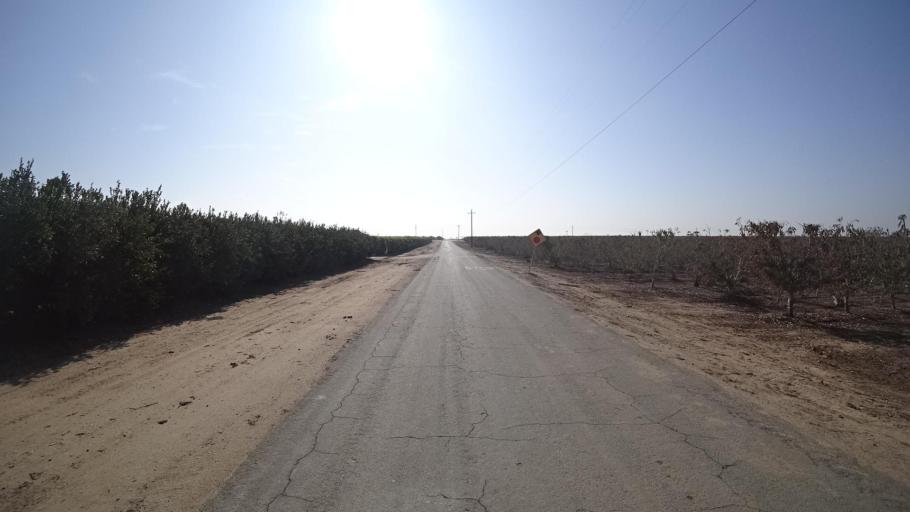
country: US
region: California
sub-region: Kern County
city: McFarland
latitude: 35.6042
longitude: -119.1865
